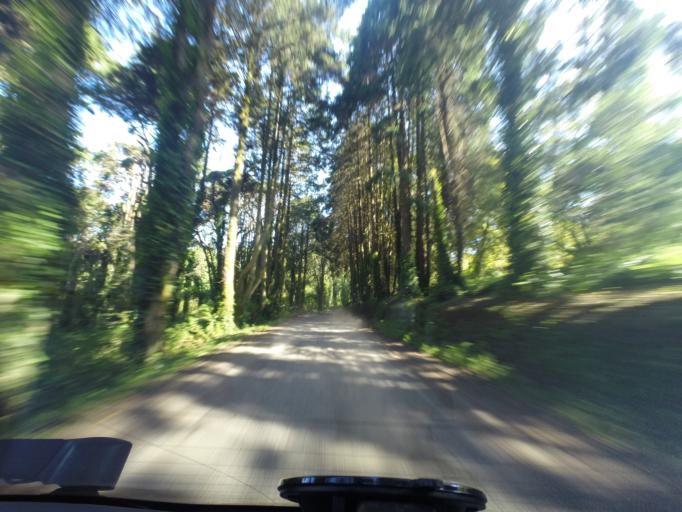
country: PT
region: Lisbon
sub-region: Sintra
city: Colares
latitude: 38.7743
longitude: -9.4568
